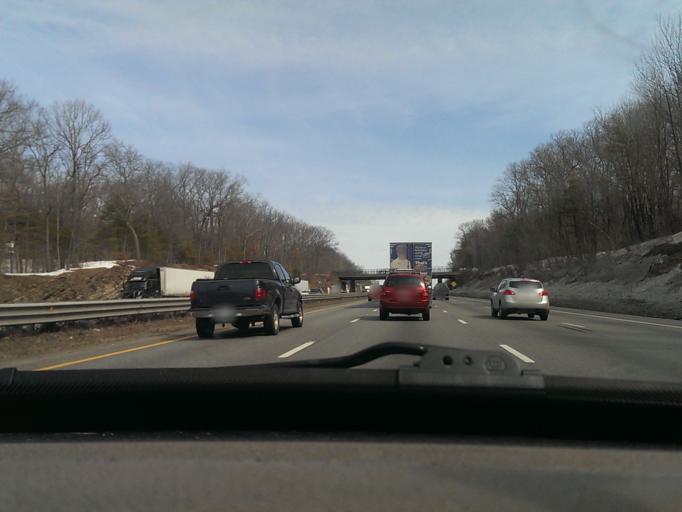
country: US
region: Massachusetts
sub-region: Worcester County
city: Sturbridge
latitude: 42.1324
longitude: -72.0508
